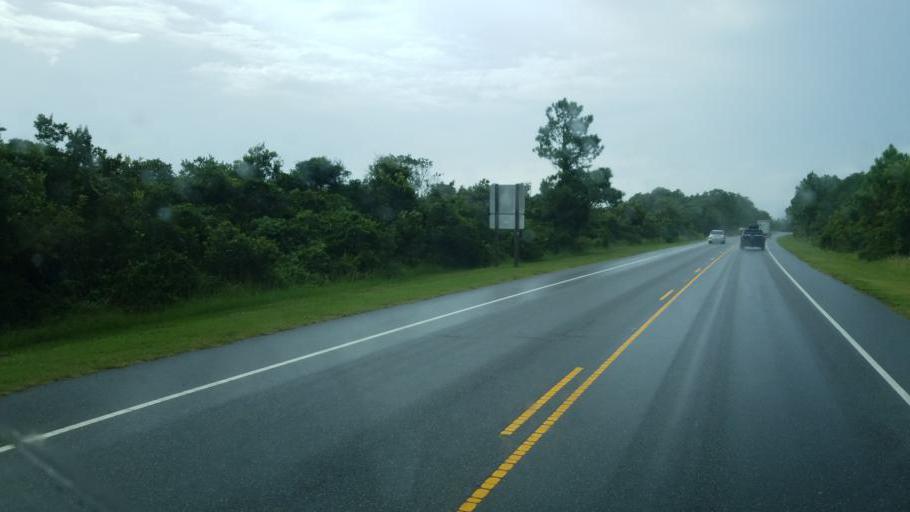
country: US
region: North Carolina
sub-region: Dare County
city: Nags Head
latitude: 35.8973
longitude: -75.5957
